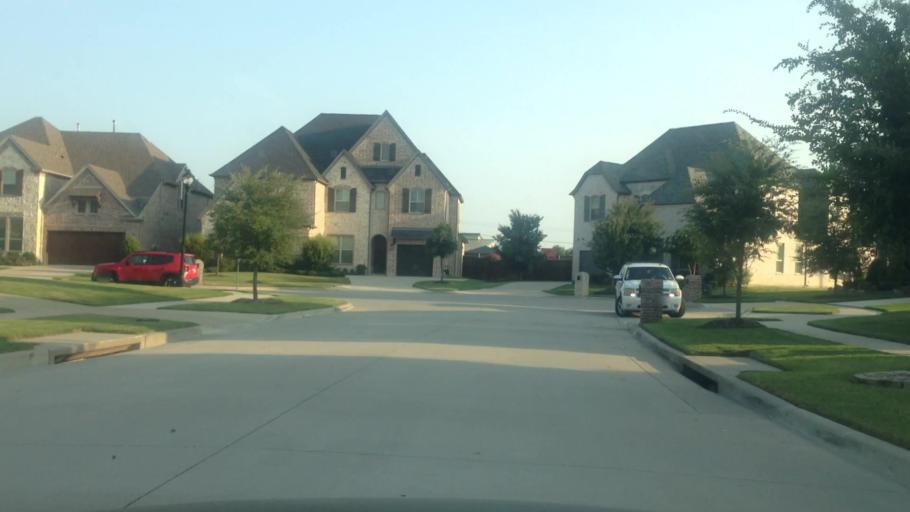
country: US
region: Texas
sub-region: Denton County
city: The Colony
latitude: 33.1313
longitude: -96.8684
